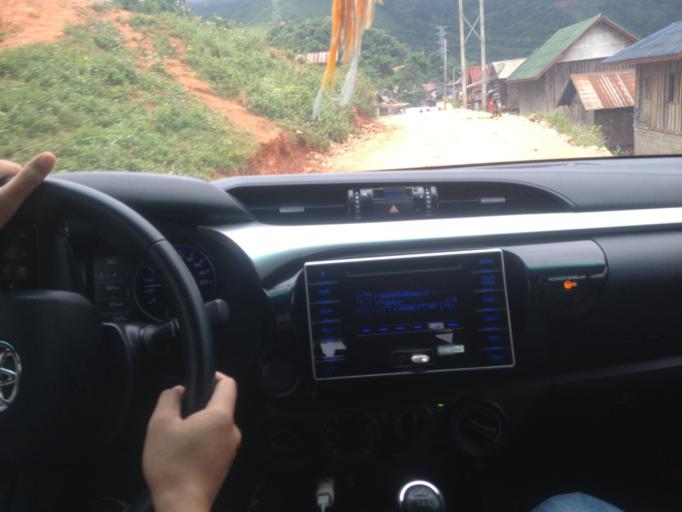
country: TH
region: Nan
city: Chaloem Phra Kiat
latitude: 19.9991
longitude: 101.1281
